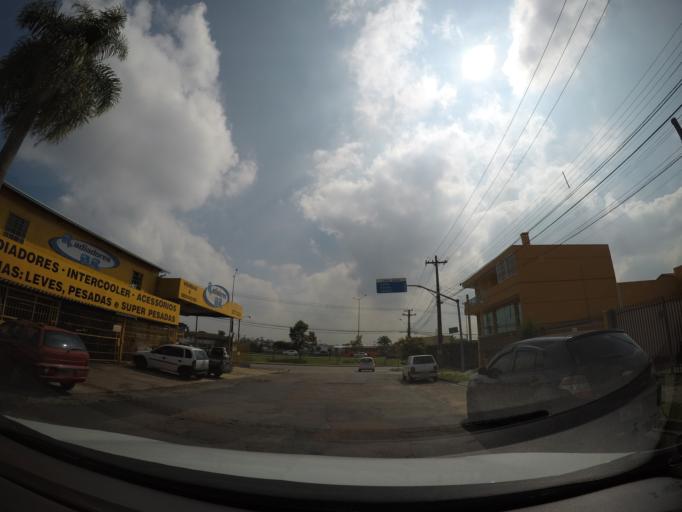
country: BR
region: Parana
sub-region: Curitiba
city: Curitiba
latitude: -25.4791
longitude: -49.2610
